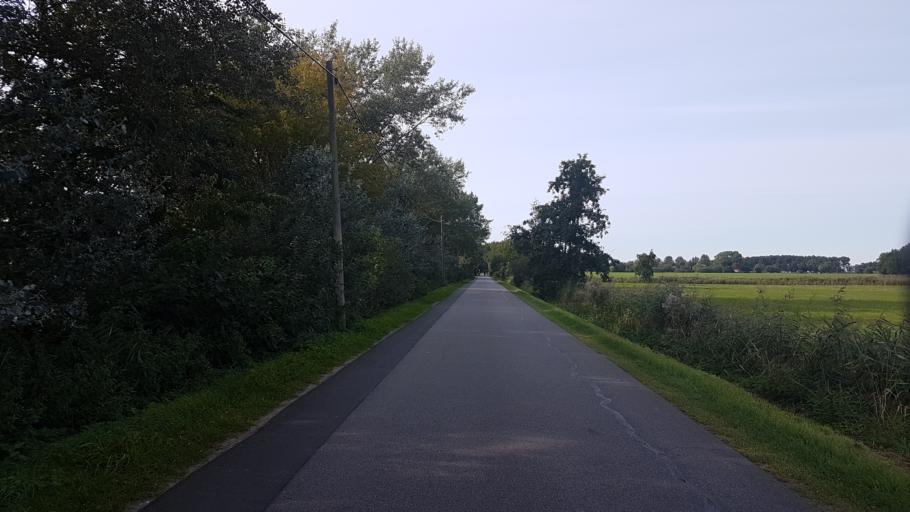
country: DE
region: Mecklenburg-Vorpommern
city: Gingst
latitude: 54.4561
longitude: 13.1413
